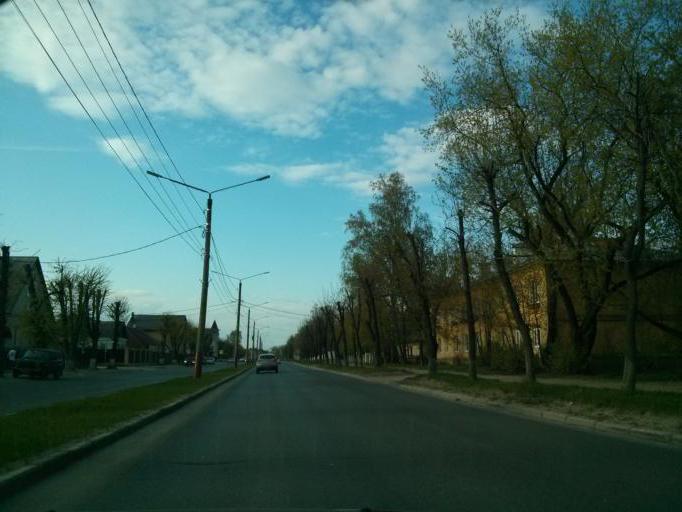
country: RU
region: Vladimir
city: Murom
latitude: 55.5806
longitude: 42.0361
